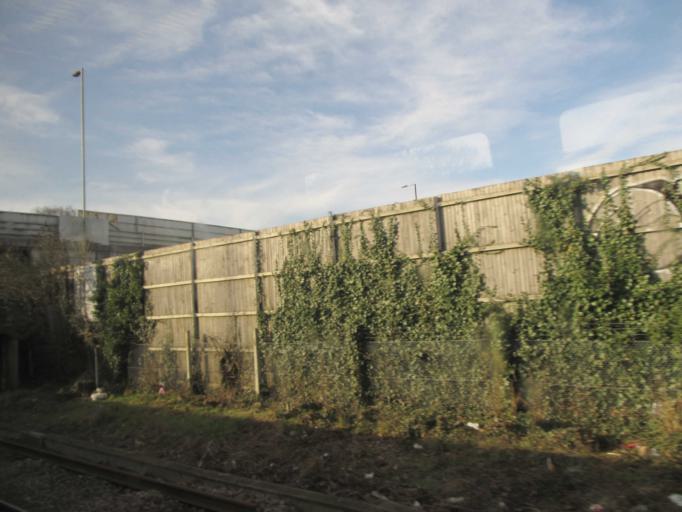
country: GB
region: England
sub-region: Hampshire
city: Farnborough
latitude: 51.2765
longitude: -0.7313
